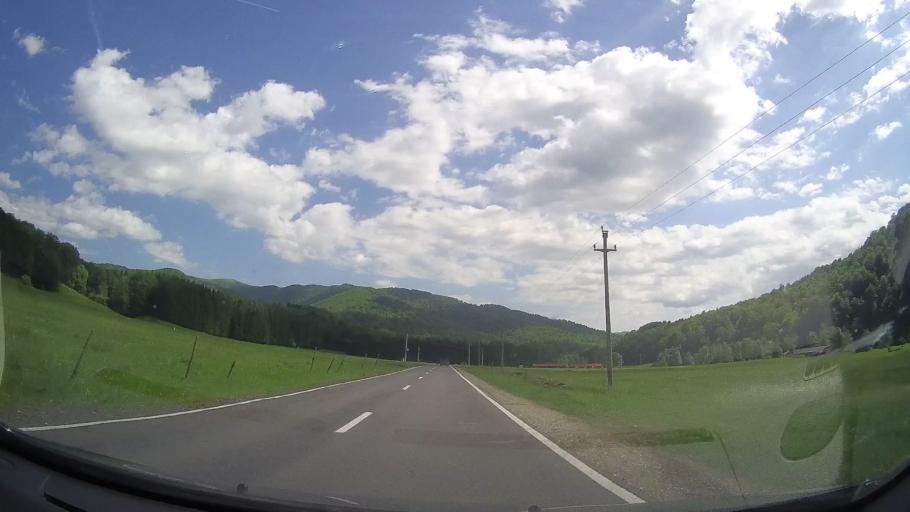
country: RO
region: Prahova
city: Maneciu
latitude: 45.4221
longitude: 25.9422
